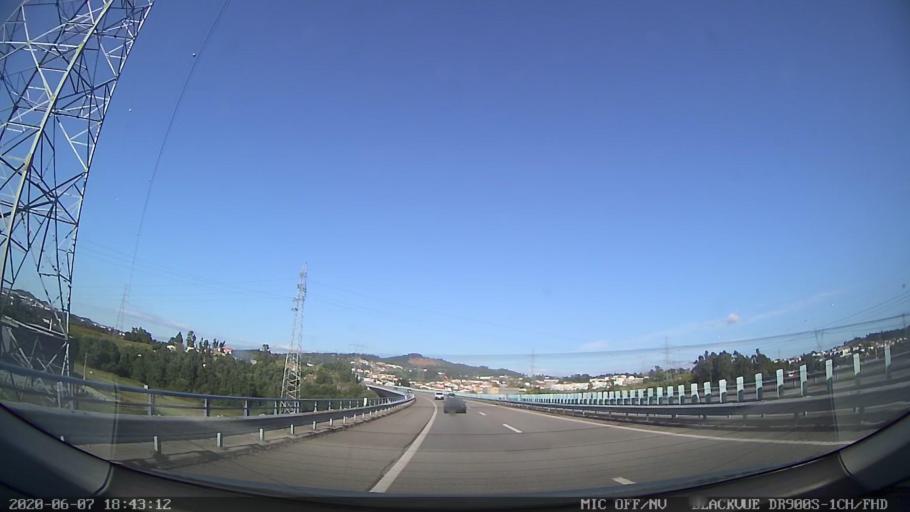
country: PT
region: Braga
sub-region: Guimaraes
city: Serzedelo
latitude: 41.4054
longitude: -8.3856
